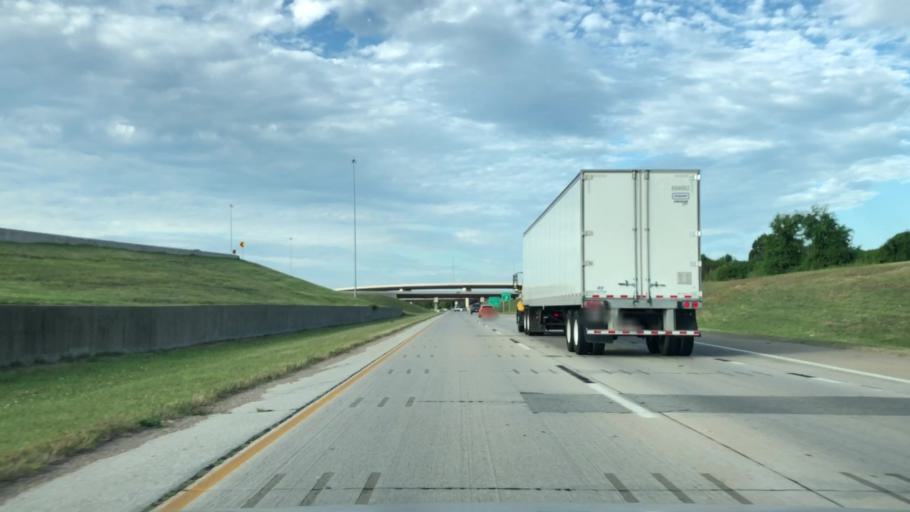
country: US
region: Oklahoma
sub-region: Tulsa County
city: Turley
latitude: 36.2027
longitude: -95.9484
